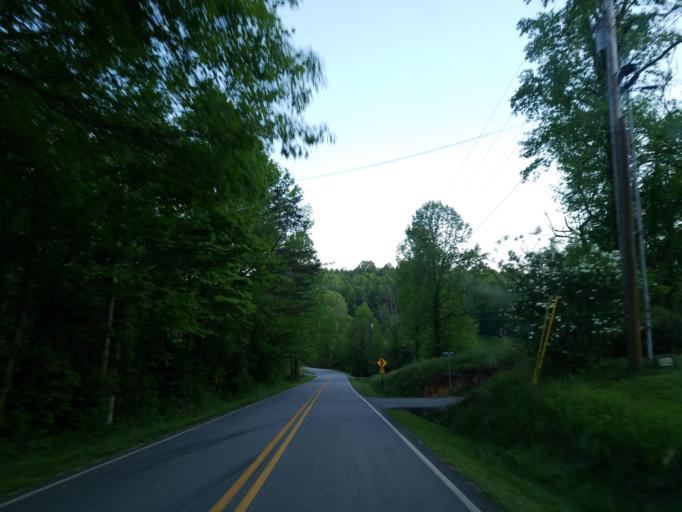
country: US
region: Georgia
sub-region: Union County
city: Blairsville
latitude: 34.7127
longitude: -83.9970
